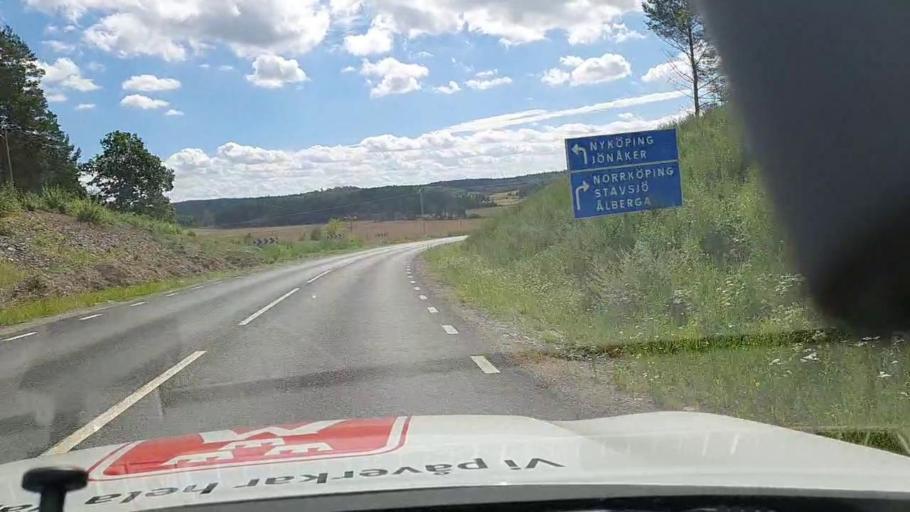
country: SE
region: Soedermanland
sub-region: Nykopings Kommun
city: Olstorp
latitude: 58.7508
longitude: 16.6161
